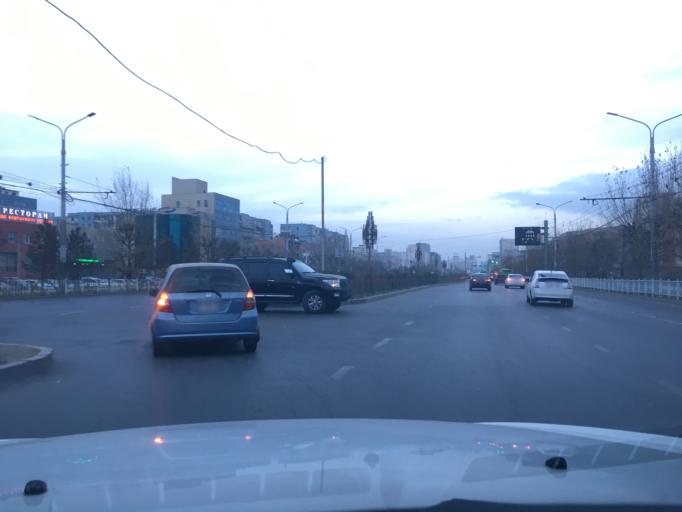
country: MN
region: Ulaanbaatar
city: Ulaanbaatar
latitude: 47.9135
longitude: 106.8642
